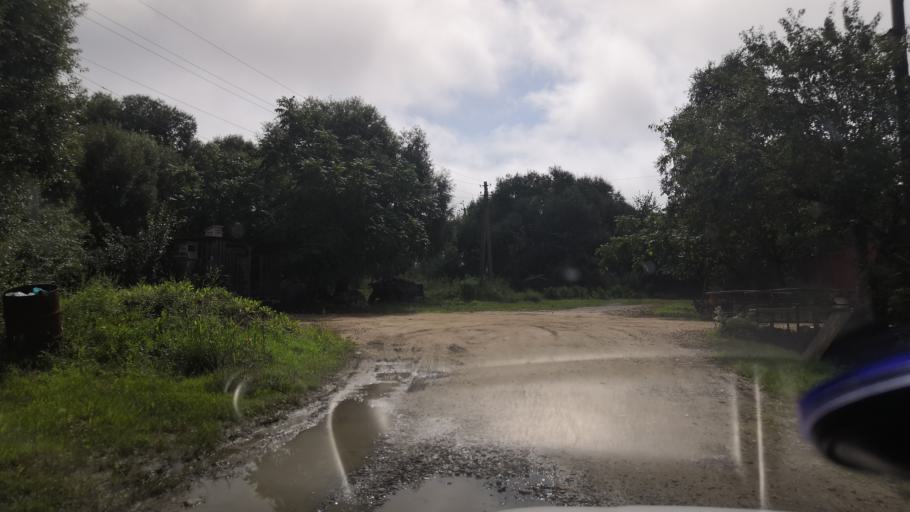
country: RU
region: Primorskiy
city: Dal'nerechensk
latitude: 45.9171
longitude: 133.7253
